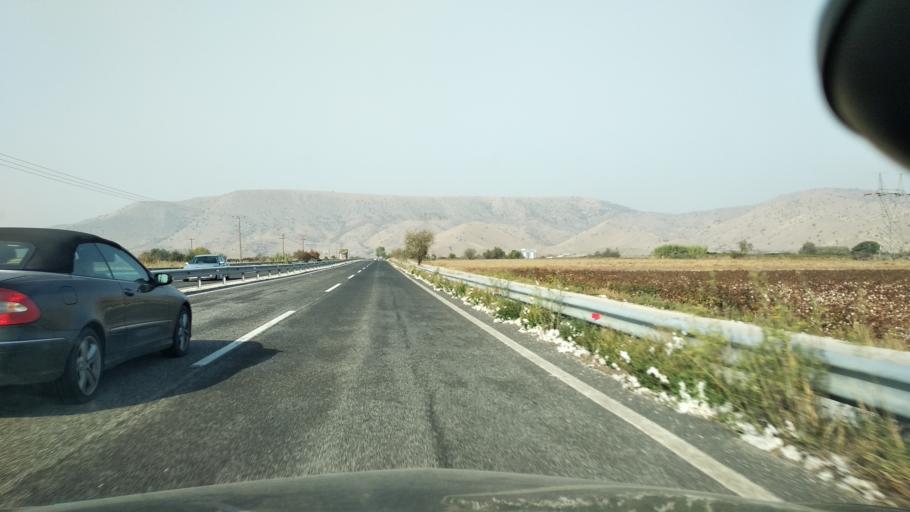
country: GR
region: Thessaly
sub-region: Trikala
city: Zarkos
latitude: 39.5959
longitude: 22.1146
